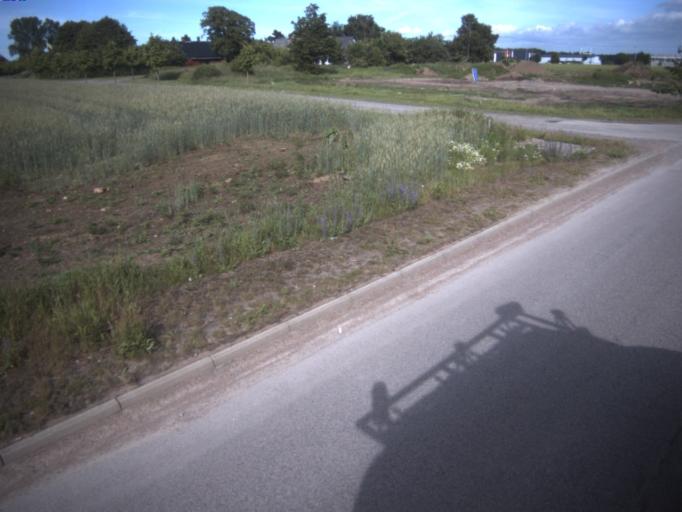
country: SE
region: Skane
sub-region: Helsingborg
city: Odakra
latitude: 56.0799
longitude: 12.7497
